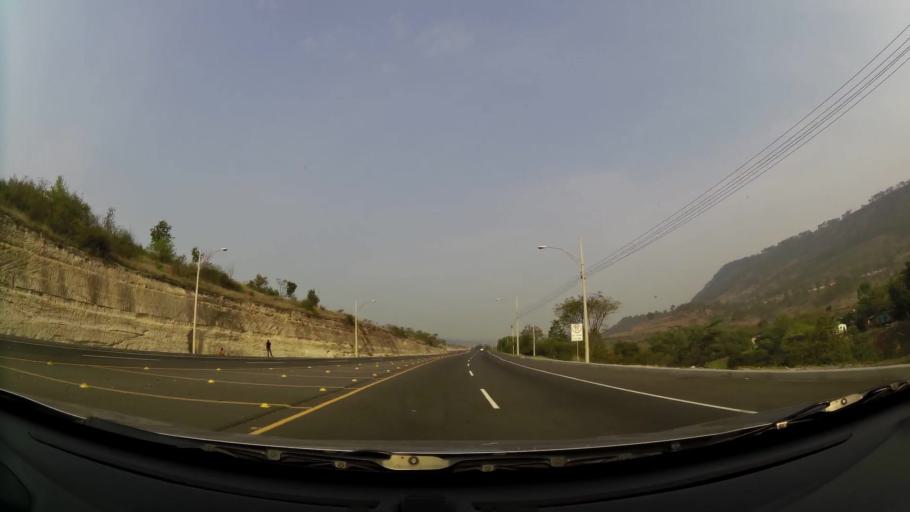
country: HN
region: Francisco Morazan
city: Zambrano
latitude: 14.2336
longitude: -87.3810
